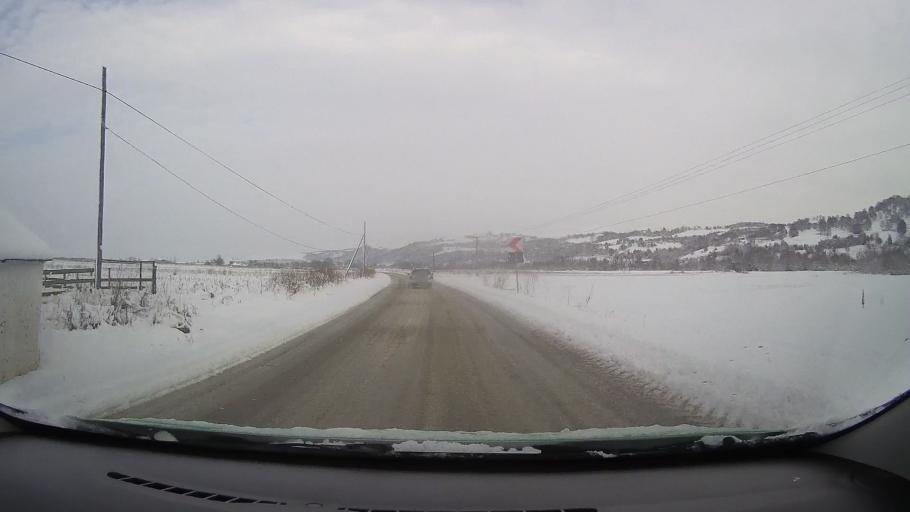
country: RO
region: Alba
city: Pianu de Sus
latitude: 45.9171
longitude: 23.4852
